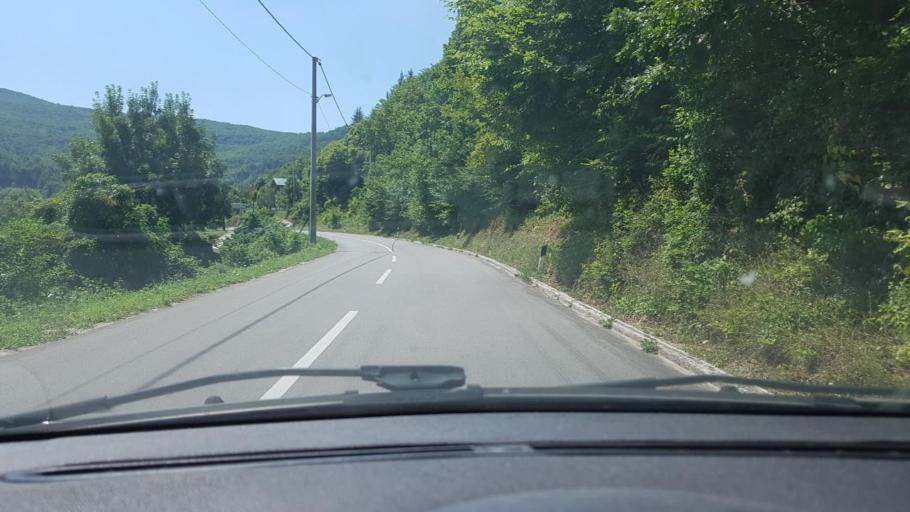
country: BA
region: Federation of Bosnia and Herzegovina
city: Orasac
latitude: 44.5662
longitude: 16.0919
